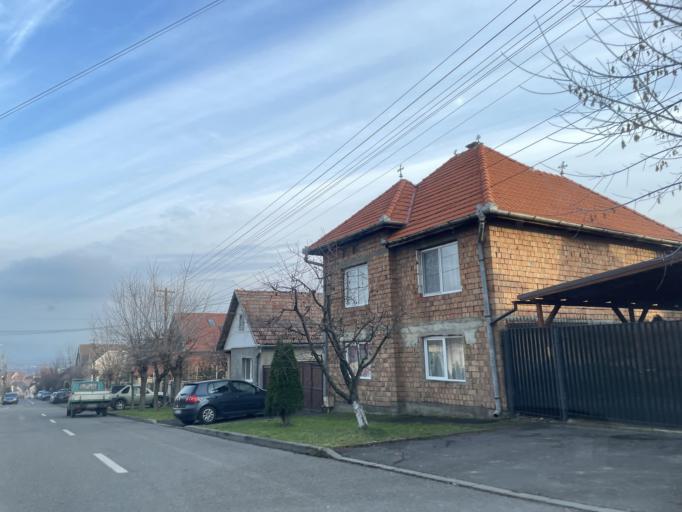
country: RO
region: Mures
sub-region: Municipiul Reghin
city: Reghin
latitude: 46.7801
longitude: 24.6932
